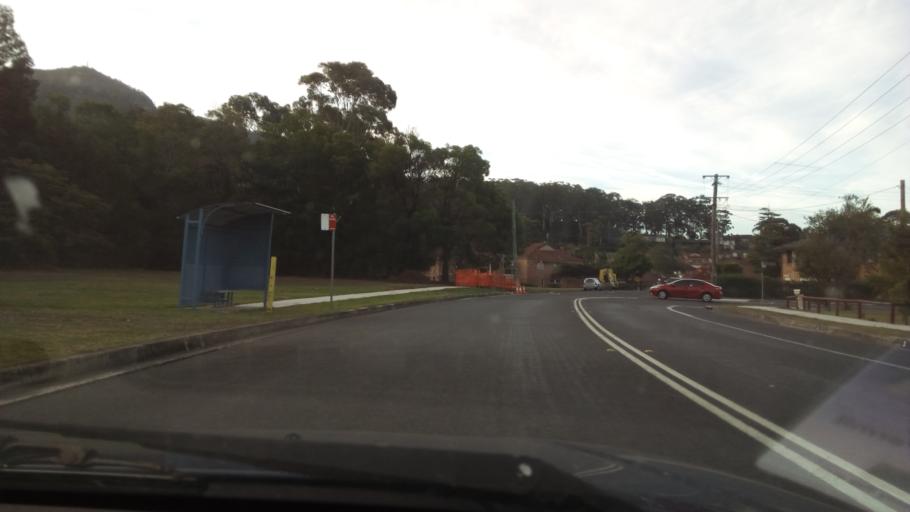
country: AU
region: New South Wales
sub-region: Wollongong
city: Mount Ousley
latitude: -34.3817
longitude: 150.8821
